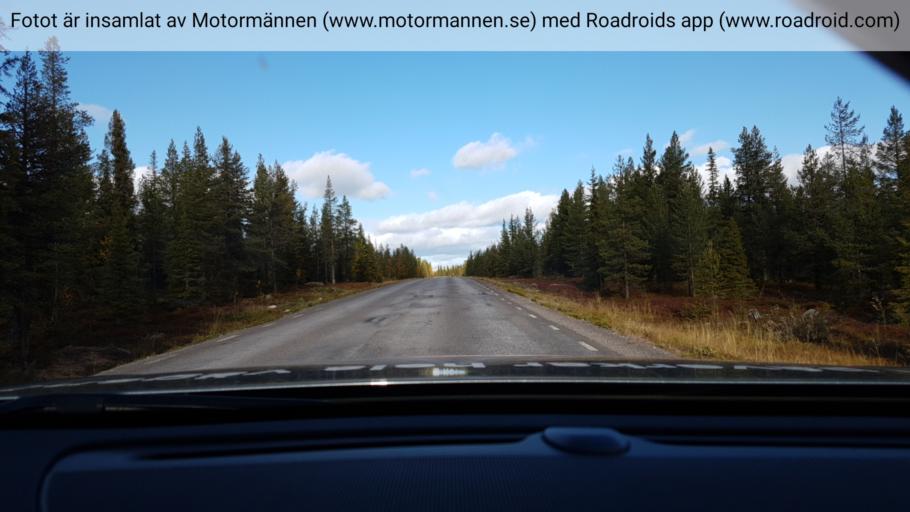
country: SE
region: Norrbotten
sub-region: Arjeplogs Kommun
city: Arjeplog
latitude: 65.8963
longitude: 18.3652
